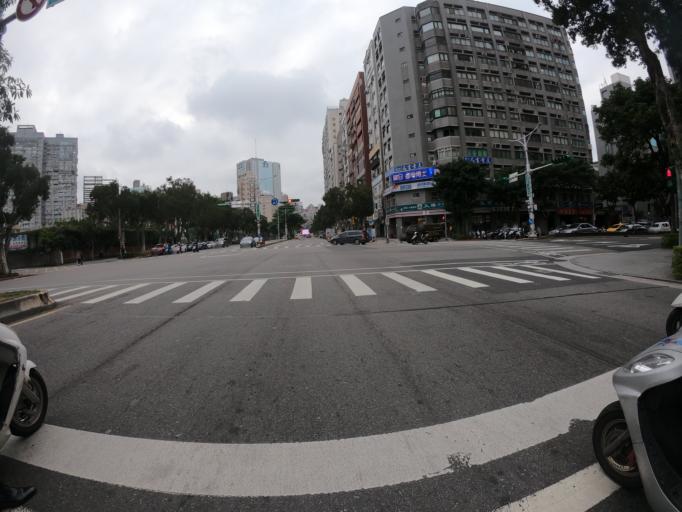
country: TW
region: Taipei
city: Taipei
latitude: 25.0268
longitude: 121.5262
